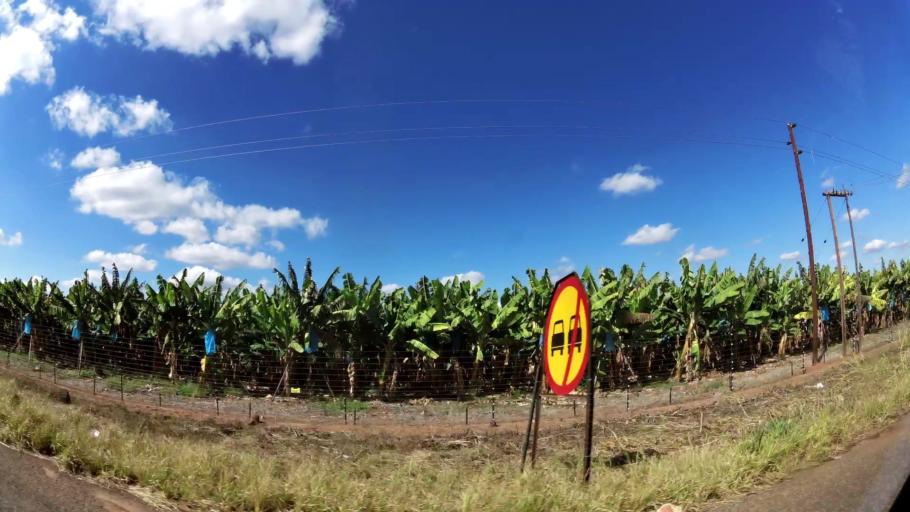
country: ZA
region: Limpopo
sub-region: Mopani District Municipality
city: Tzaneen
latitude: -23.8107
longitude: 30.1748
